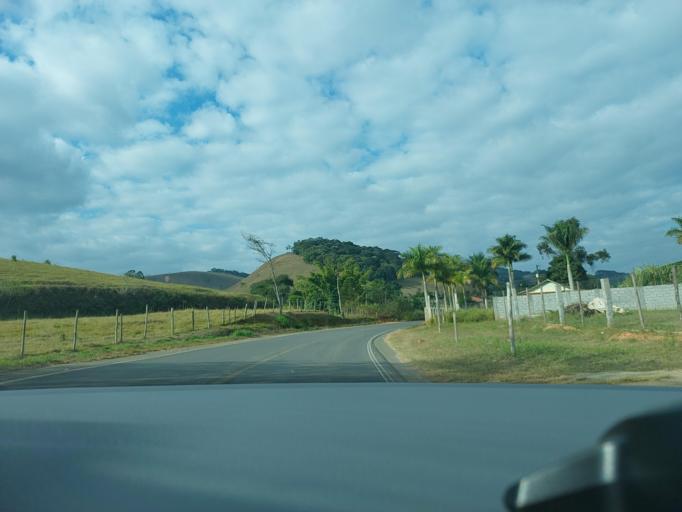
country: BR
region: Minas Gerais
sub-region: Vicosa
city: Vicosa
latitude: -20.8258
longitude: -42.7346
